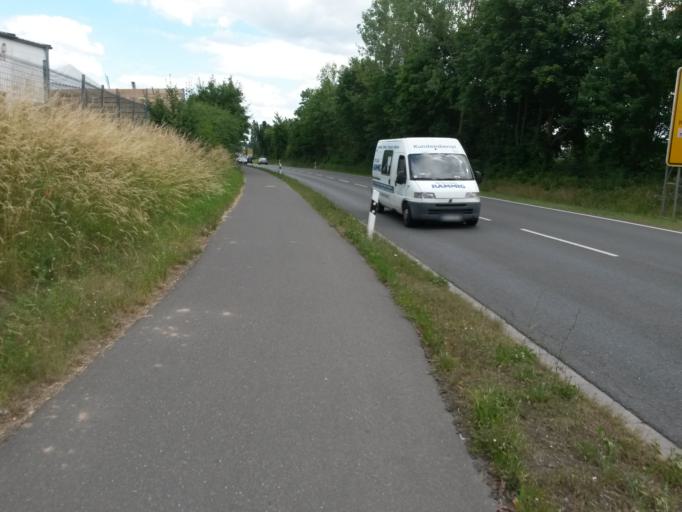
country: DE
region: Bavaria
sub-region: Regierungsbezirk Mittelfranken
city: Seukendorf
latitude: 49.4779
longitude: 10.8679
